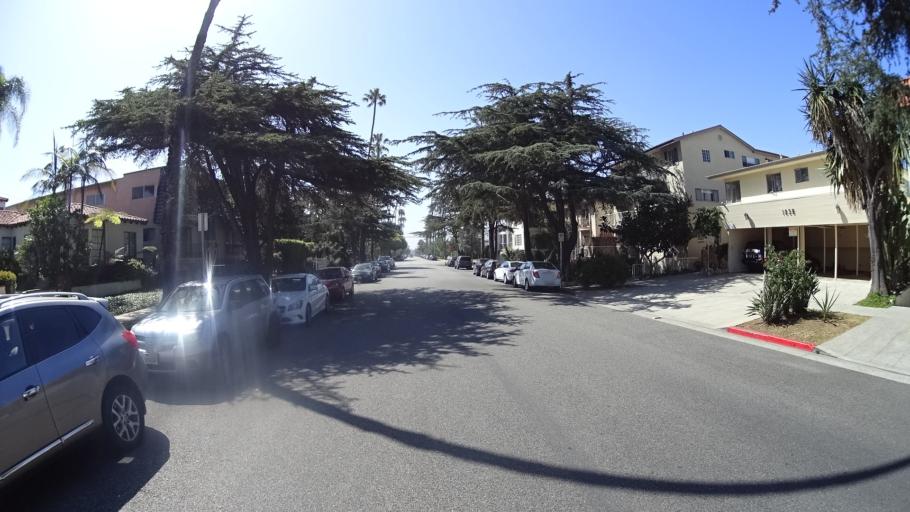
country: US
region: California
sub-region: Los Angeles County
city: Santa Monica
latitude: 34.0250
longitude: -118.4960
